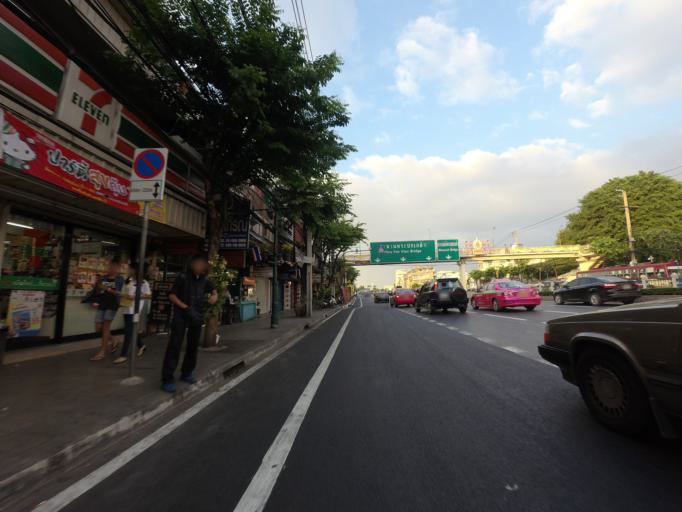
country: TH
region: Bangkok
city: Thon Buri
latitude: 13.7333
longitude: 100.4954
